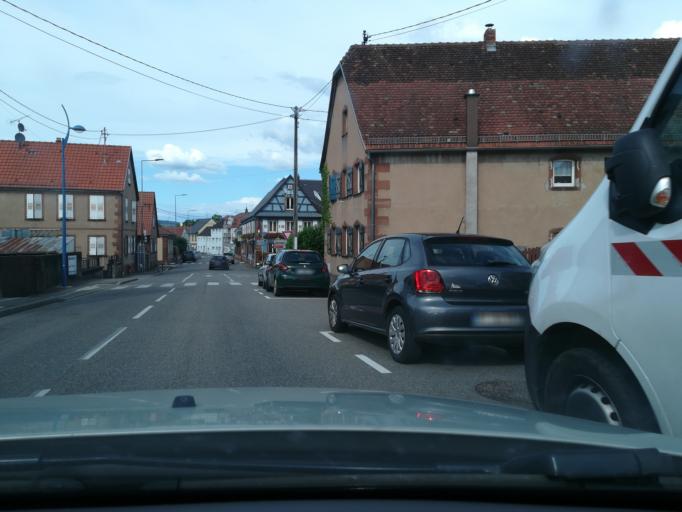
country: FR
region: Alsace
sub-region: Departement du Bas-Rhin
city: Ingwiller
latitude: 48.8685
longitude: 7.4791
